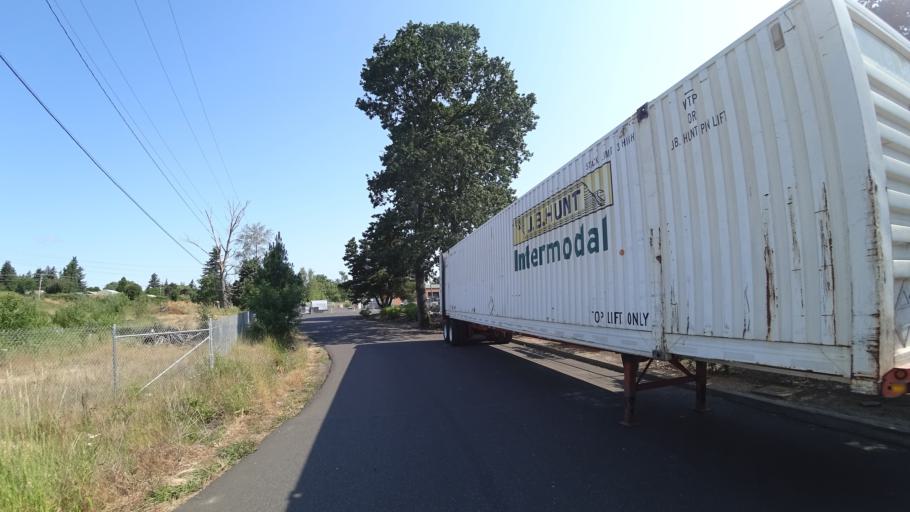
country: US
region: Oregon
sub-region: Multnomah County
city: Lents
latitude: 45.4590
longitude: -122.5845
